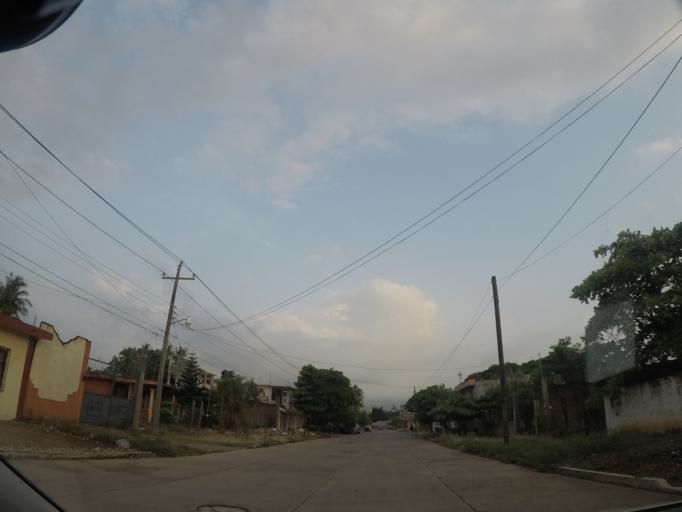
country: MX
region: Oaxaca
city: Matias Romero
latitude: 16.8737
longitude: -95.0366
